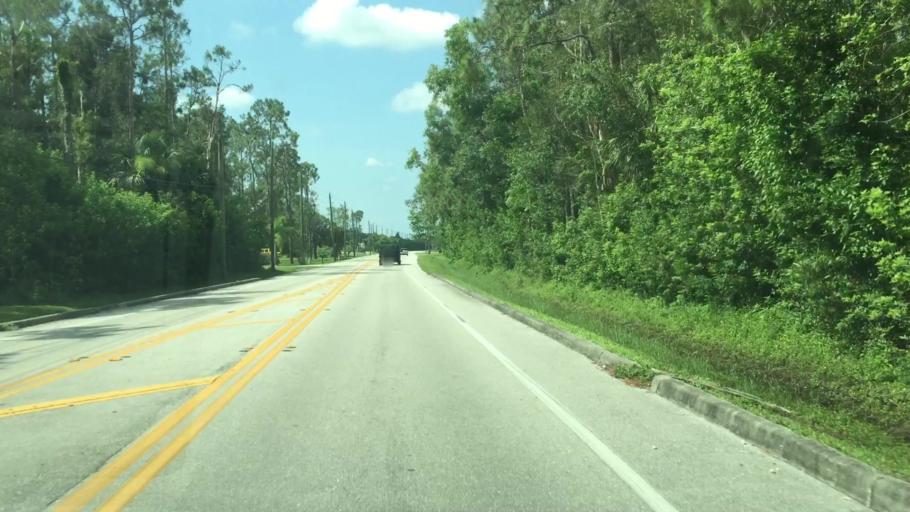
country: US
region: Florida
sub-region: Lee County
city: Villas
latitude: 26.5573
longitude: -81.8468
